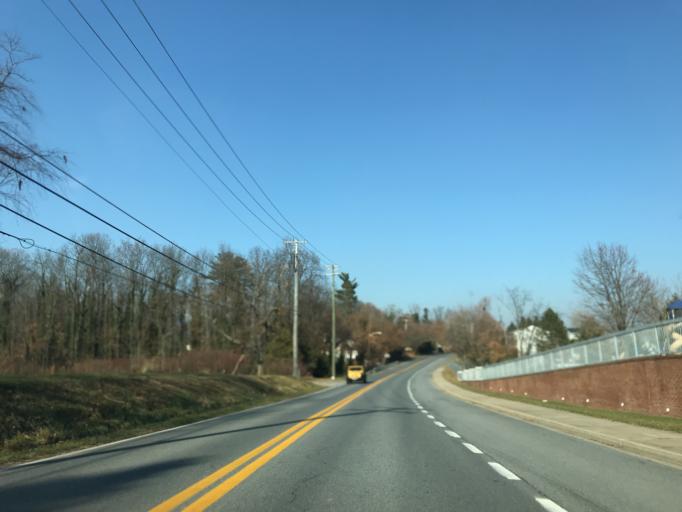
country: US
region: Maryland
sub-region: Carroll County
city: Taneytown
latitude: 39.6521
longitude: -77.1719
